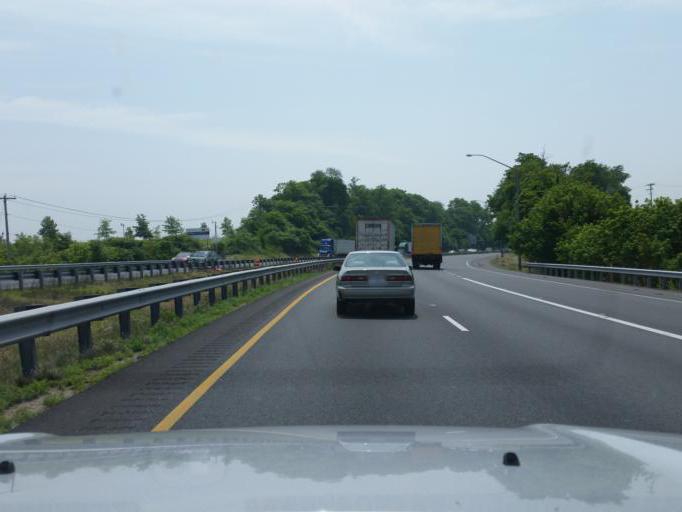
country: US
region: Maryland
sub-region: Frederick County
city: Urbana
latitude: 39.3223
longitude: -77.3552
